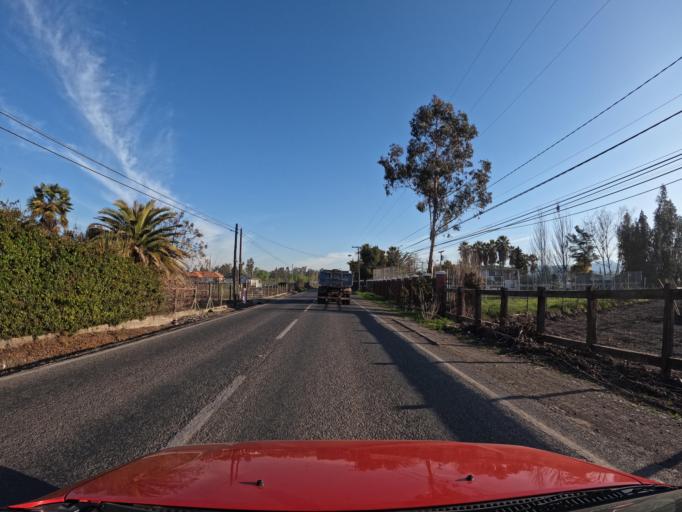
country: CL
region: Maule
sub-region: Provincia de Curico
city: Rauco
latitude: -34.8779
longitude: -71.2687
